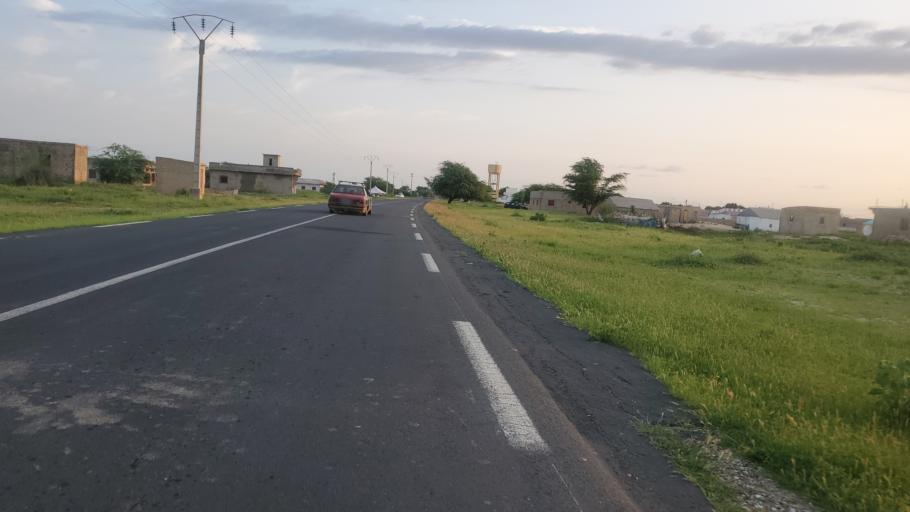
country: SN
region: Saint-Louis
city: Saint-Louis
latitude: 16.1391
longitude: -16.4101
